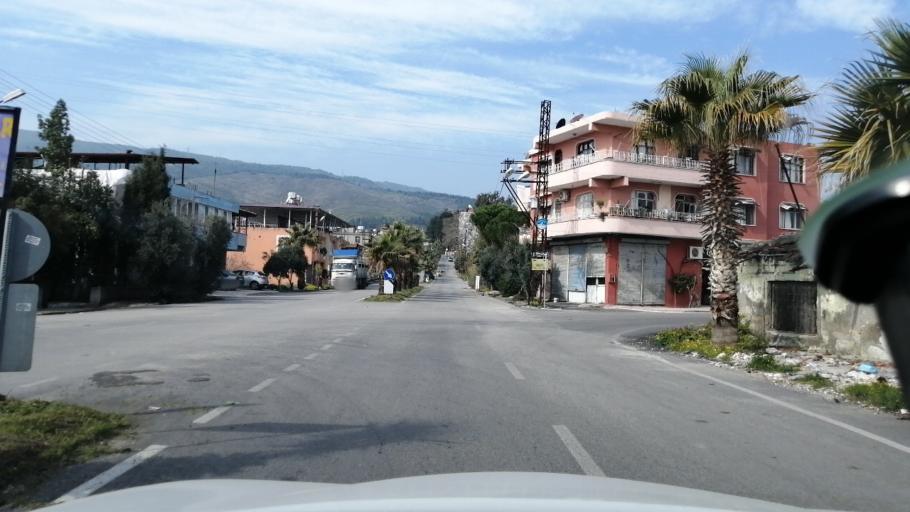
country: TR
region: Hatay
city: Serinyol
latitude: 36.3526
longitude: 36.2105
